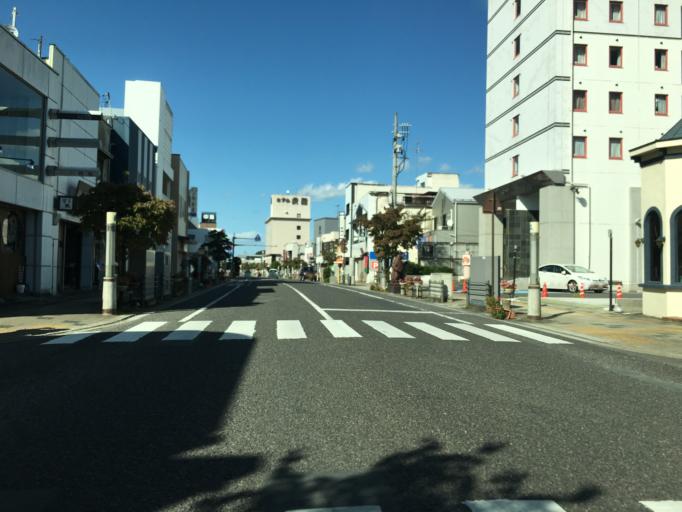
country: JP
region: Fukushima
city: Sukagawa
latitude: 37.2879
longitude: 140.3755
